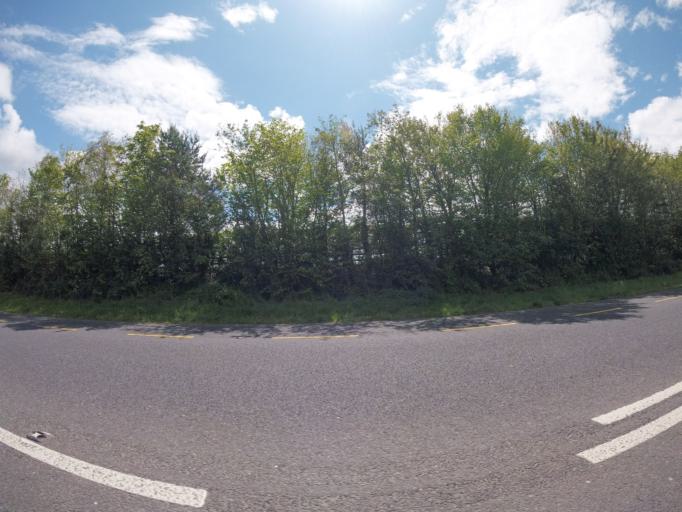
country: IE
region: Munster
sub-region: Waterford
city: Portlaw
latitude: 52.1989
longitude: -7.4190
